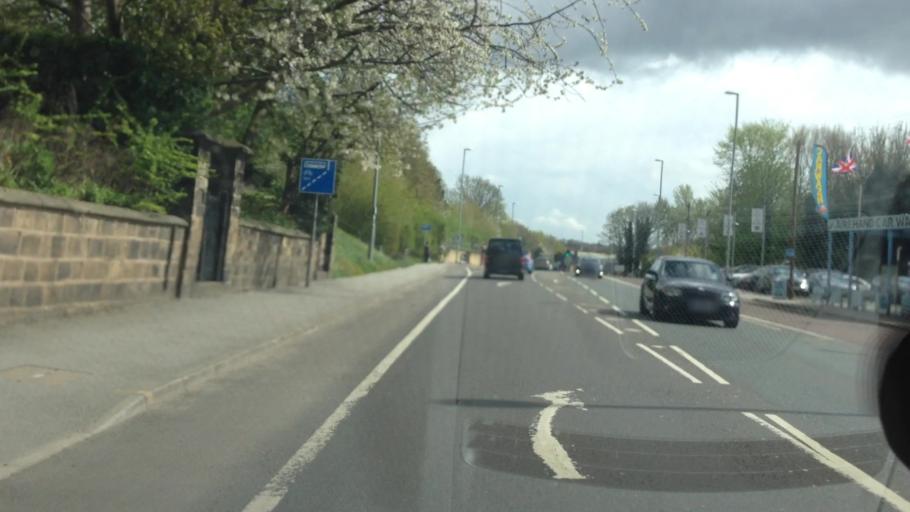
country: GB
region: England
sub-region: City and Borough of Leeds
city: Horsforth
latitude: 53.8142
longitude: -1.6003
